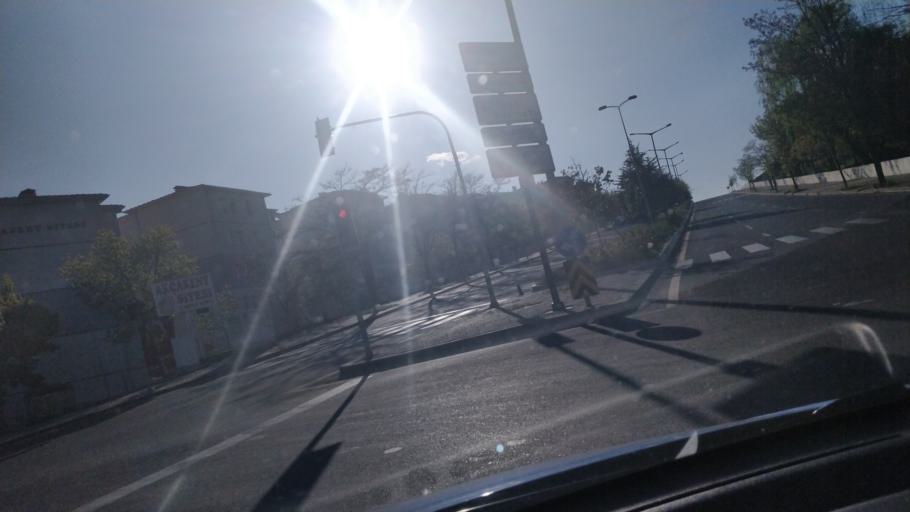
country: TR
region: Ankara
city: Batikent
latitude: 39.9583
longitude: 32.7204
